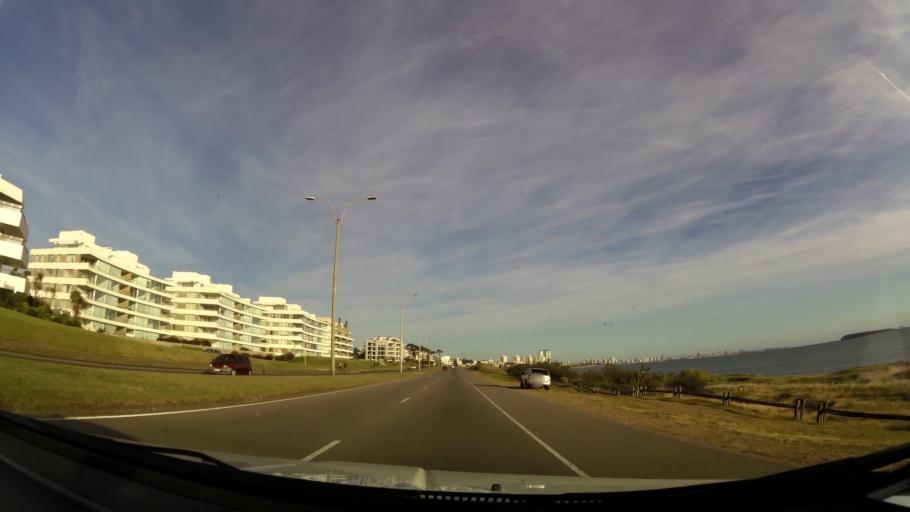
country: UY
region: Maldonado
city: Maldonado
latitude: -34.9158
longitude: -54.9798
